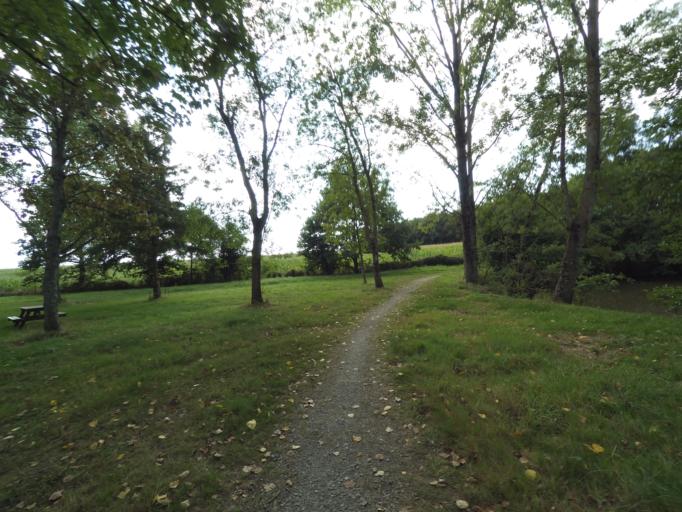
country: FR
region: Pays de la Loire
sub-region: Departement de la Loire-Atlantique
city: Vieillevigne
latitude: 46.9561
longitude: -1.4314
